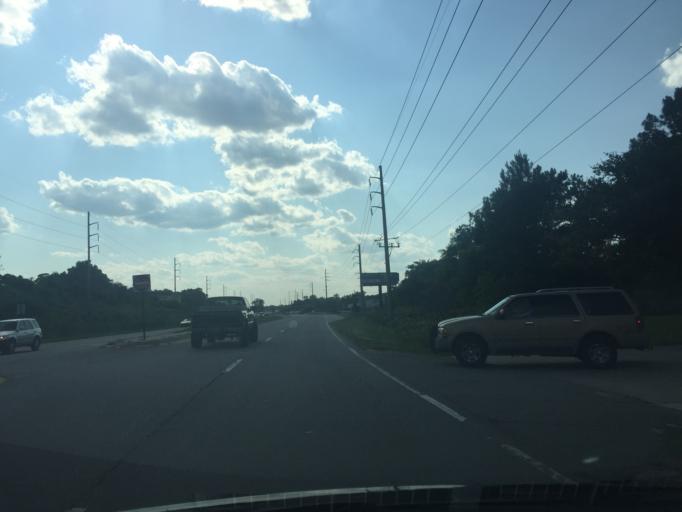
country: US
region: Georgia
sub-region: Chatham County
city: Savannah
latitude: 32.0717
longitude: -81.0651
